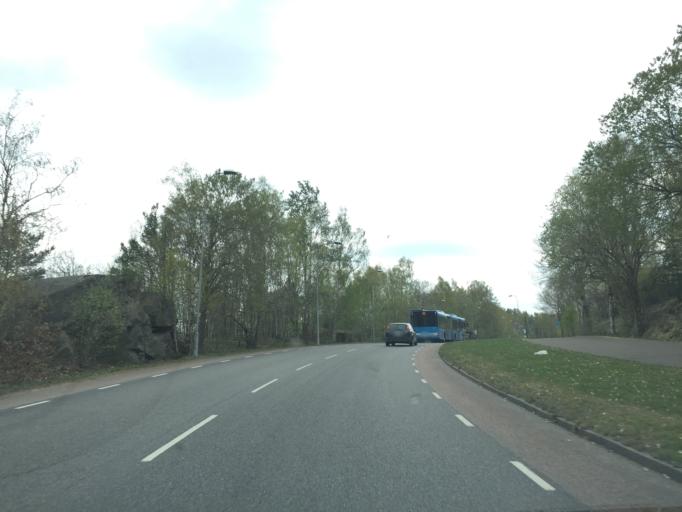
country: SE
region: Vaestra Goetaland
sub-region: Goteborg
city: Loevgaerdet
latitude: 57.8170
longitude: 12.0310
